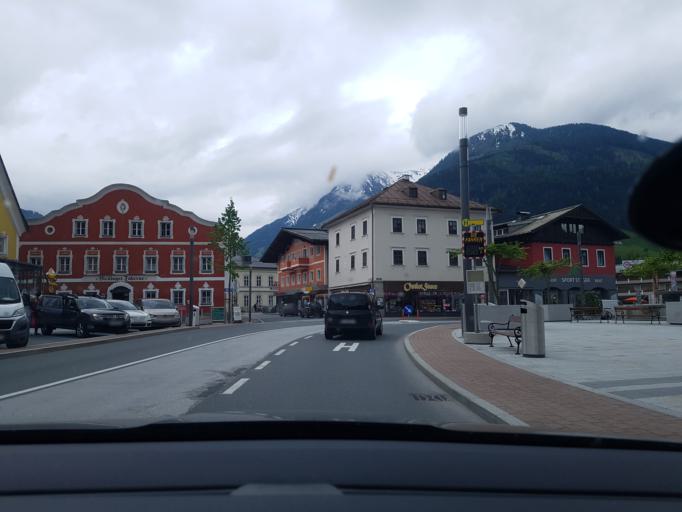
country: AT
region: Salzburg
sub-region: Politischer Bezirk Zell am See
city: Mittersill
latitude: 47.2813
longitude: 12.4821
